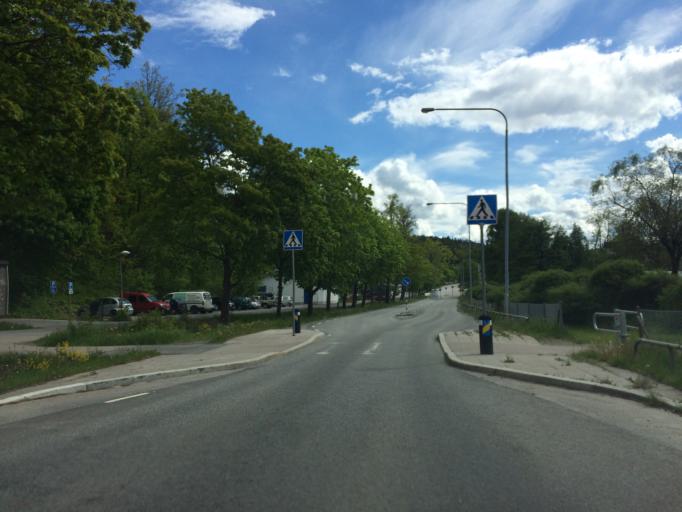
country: SE
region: Stockholm
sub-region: Botkyrka Kommun
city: Fittja
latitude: 59.2591
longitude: 17.8799
